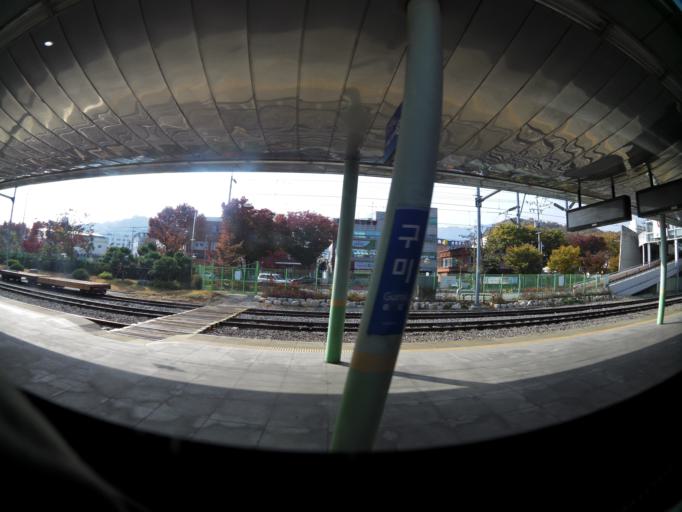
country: KR
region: Gyeongsangbuk-do
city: Gumi
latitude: 36.1277
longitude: 128.3323
